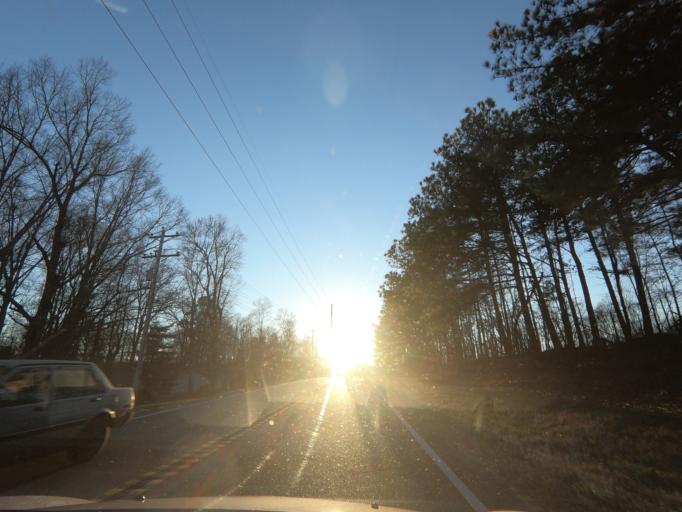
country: US
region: Georgia
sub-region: Forsyth County
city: Cumming
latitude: 34.2986
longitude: -84.1582
